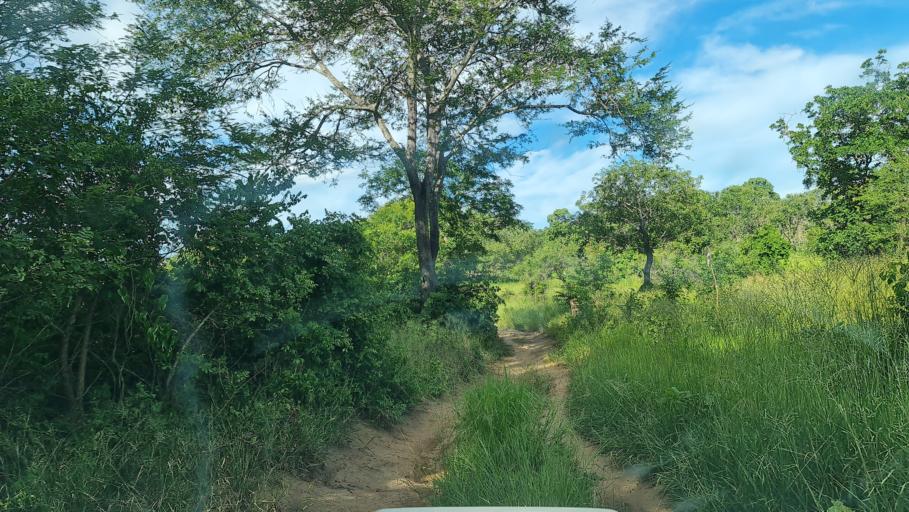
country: MZ
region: Nampula
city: Ilha de Mocambique
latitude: -15.5042
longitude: 40.1559
